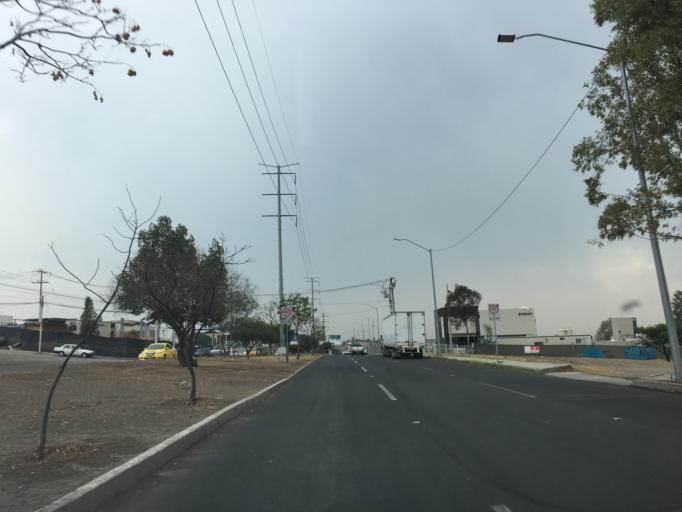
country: MX
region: Queretaro
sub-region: Queretaro
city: Santiago de Queretaro
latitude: 20.5794
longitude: -100.3683
